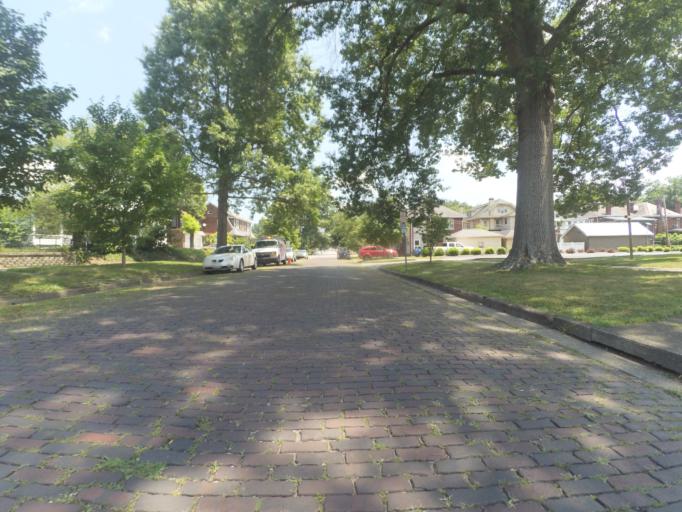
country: US
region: West Virginia
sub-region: Cabell County
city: Huntington
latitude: 38.4092
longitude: -82.4433
